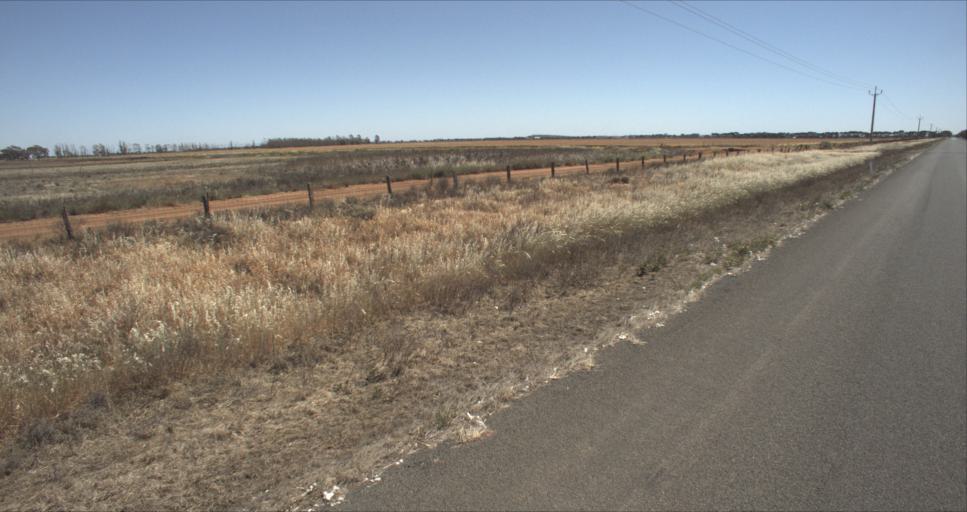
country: AU
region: New South Wales
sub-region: Leeton
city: Leeton
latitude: -34.4881
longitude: 146.2892
